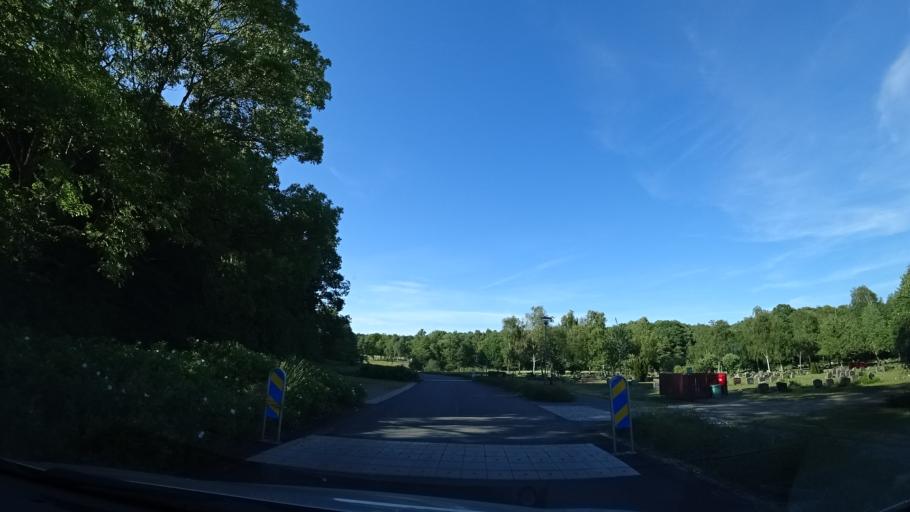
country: SE
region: Vaestra Goetaland
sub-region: Goteborg
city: Billdal
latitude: 57.5803
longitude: 11.9784
